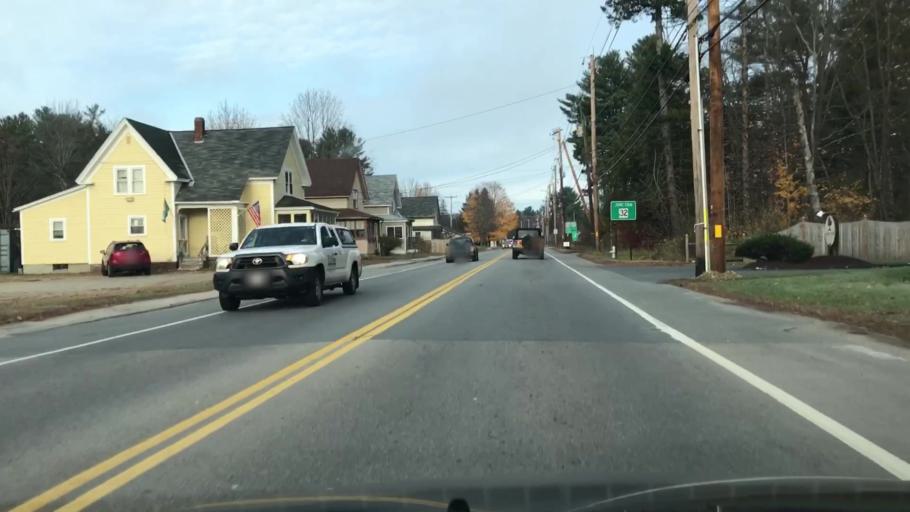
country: US
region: New Hampshire
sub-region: Cheshire County
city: Keene
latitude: 42.9112
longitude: -72.2636
